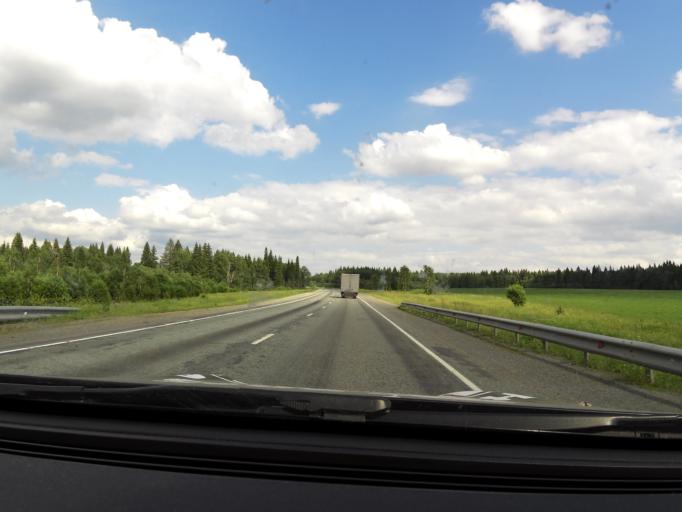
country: RU
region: Sverdlovsk
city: Bisert'
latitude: 56.8256
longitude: 59.1672
